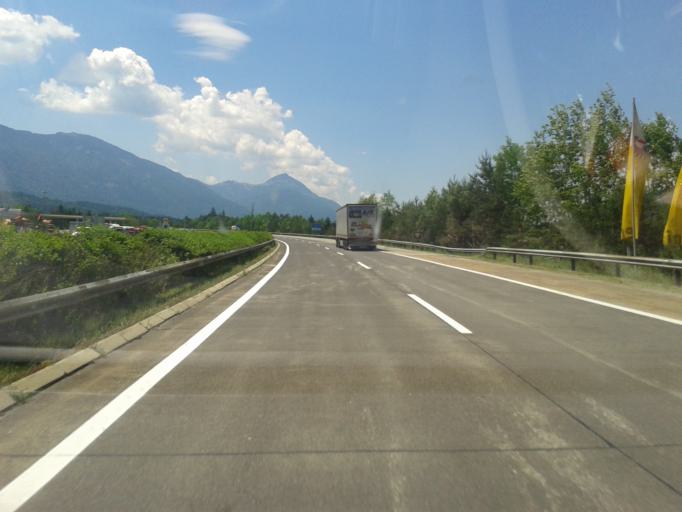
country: AT
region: Carinthia
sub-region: Politischer Bezirk Villach Land
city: Arnoldstein
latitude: 46.5704
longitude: 13.7018
